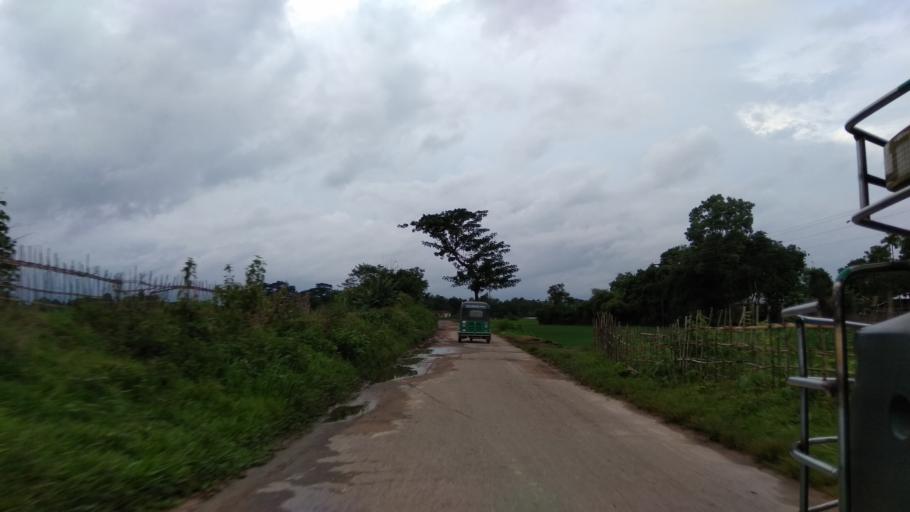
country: IN
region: Tripura
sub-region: Dhalai
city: Kamalpur
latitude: 24.2109
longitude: 91.8600
